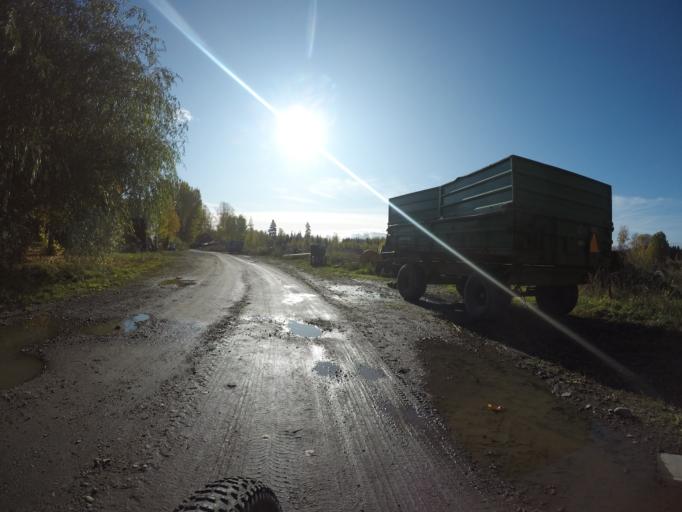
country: SE
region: Vaestmanland
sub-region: Kungsors Kommun
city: Kungsoer
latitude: 59.3166
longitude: 16.0973
